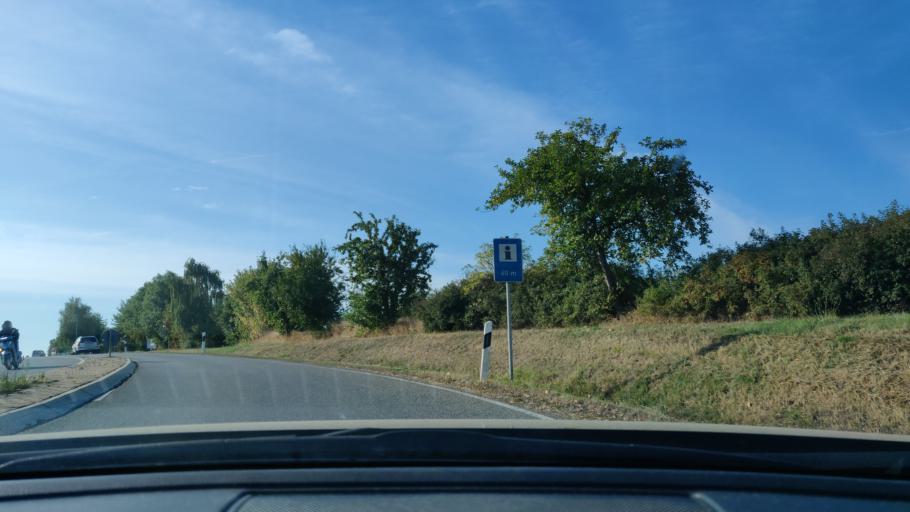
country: DE
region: Hesse
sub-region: Regierungsbezirk Kassel
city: Bad Wildungen
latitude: 51.1336
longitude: 9.1223
